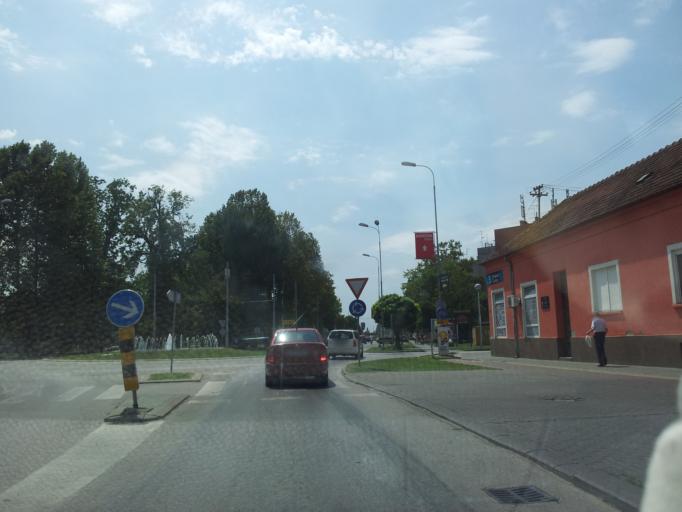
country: HR
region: Osjecko-Baranjska
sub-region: Grad Osijek
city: Osijek
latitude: 45.5466
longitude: 18.6789
